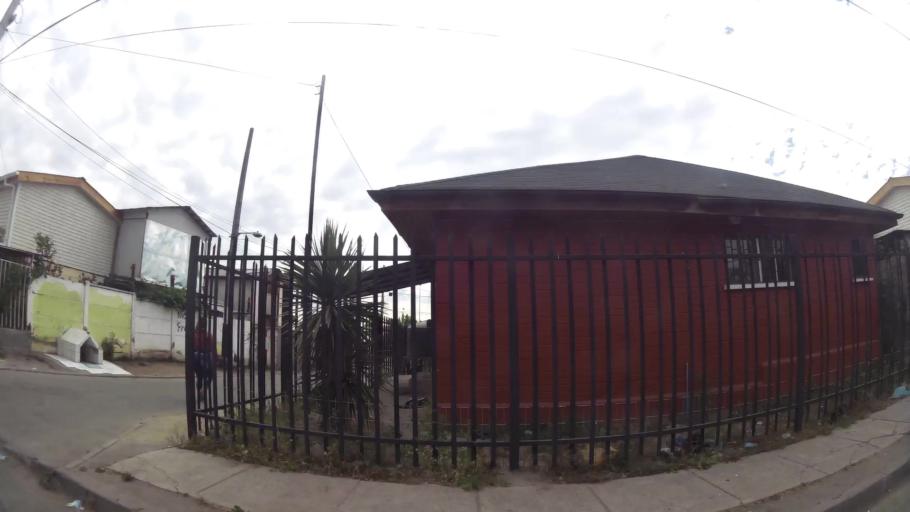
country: CL
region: Santiago Metropolitan
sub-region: Provincia de Santiago
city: La Pintana
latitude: -33.6152
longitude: -70.6230
